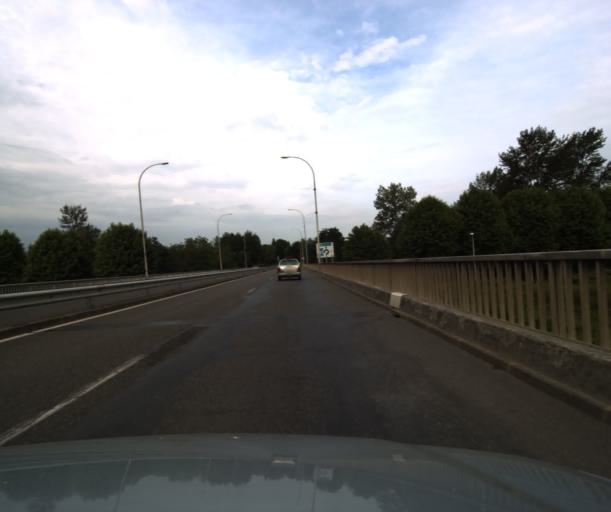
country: FR
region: Midi-Pyrenees
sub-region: Departement des Hautes-Pyrenees
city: Tarbes
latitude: 43.2291
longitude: 0.0911
